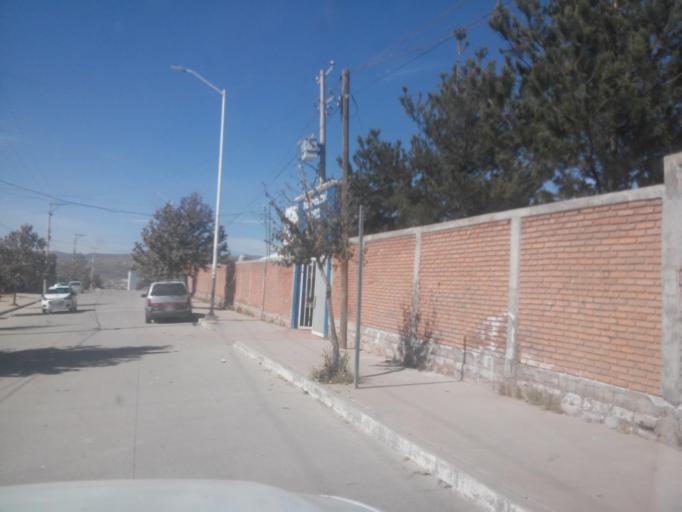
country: MX
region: Durango
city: Victoria de Durango
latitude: 24.0641
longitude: -104.6770
